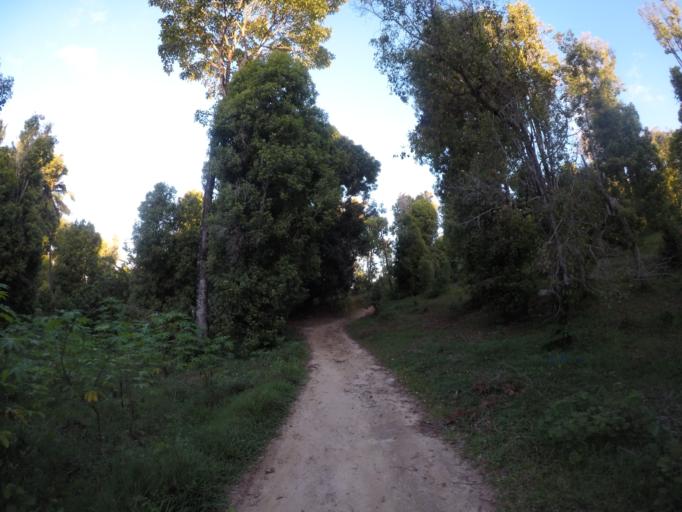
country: TZ
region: Pemba South
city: Mtambile
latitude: -5.3797
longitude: 39.7108
